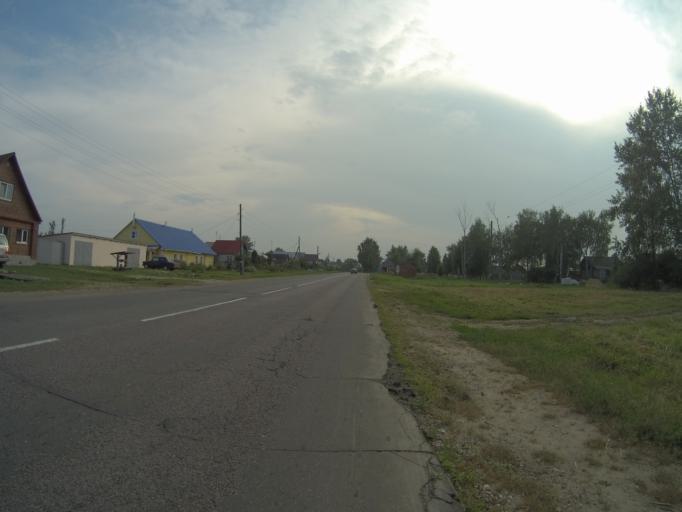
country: RU
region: Vladimir
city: Suzdal'
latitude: 56.4058
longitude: 40.3451
